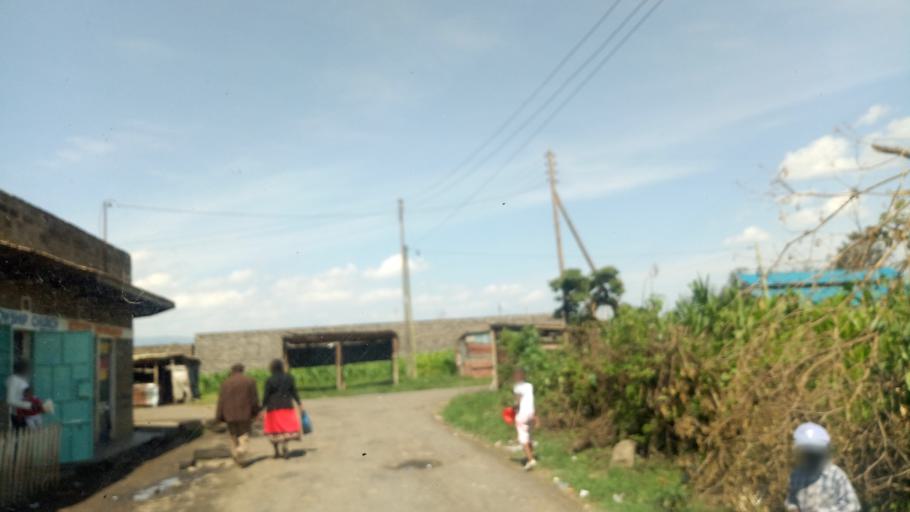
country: KE
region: Nakuru
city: Nakuru
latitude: -0.2784
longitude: 36.1175
